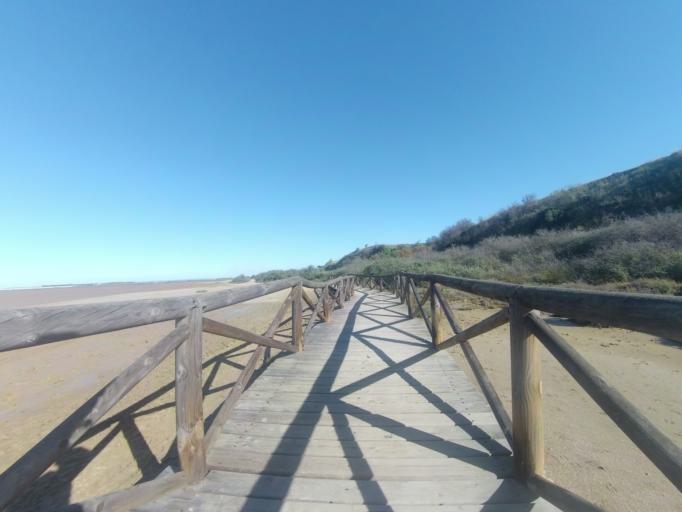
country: ES
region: Andalusia
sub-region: Provincia de Huelva
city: Palos de la Frontera
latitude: 37.2366
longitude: -6.8929
